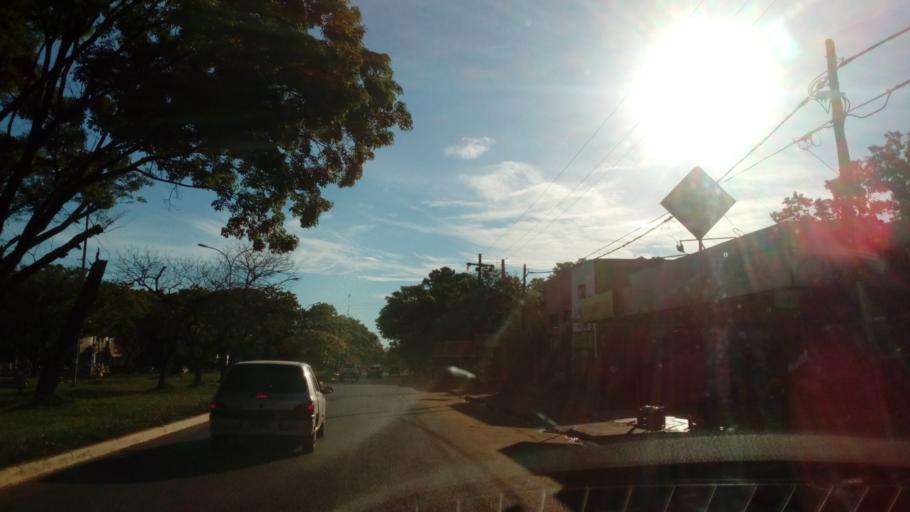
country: AR
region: Misiones
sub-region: Departamento de Capital
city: Posadas
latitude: -27.4321
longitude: -55.8850
